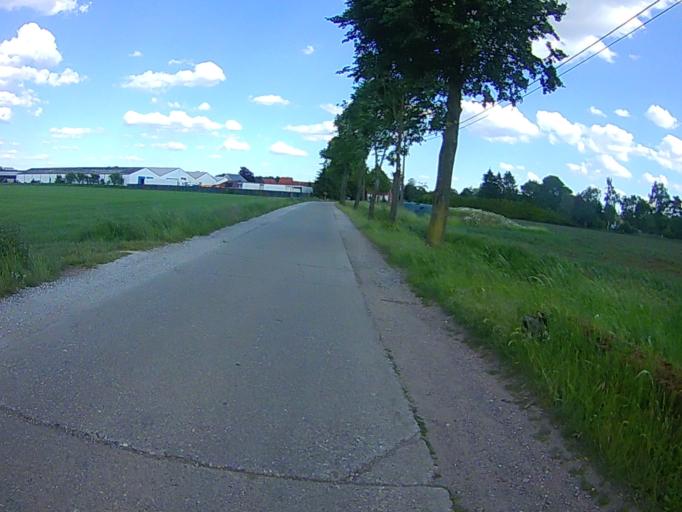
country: BE
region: Flanders
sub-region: Provincie Antwerpen
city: Lille
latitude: 51.2222
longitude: 4.8632
